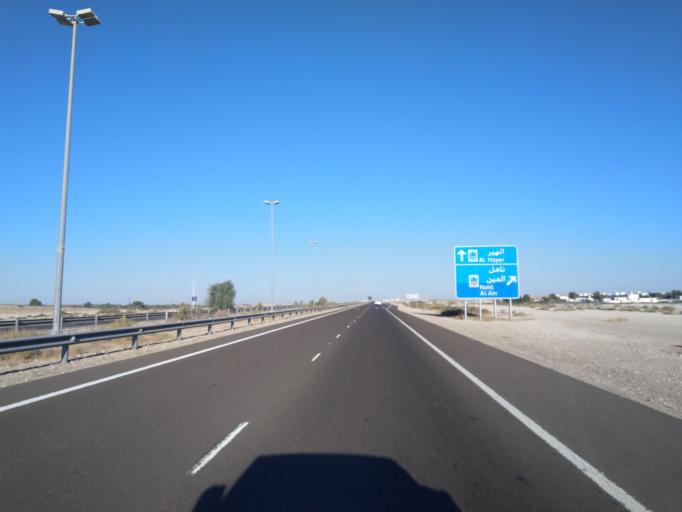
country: OM
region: Al Buraimi
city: Al Buraymi
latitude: 24.5243
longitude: 55.5442
